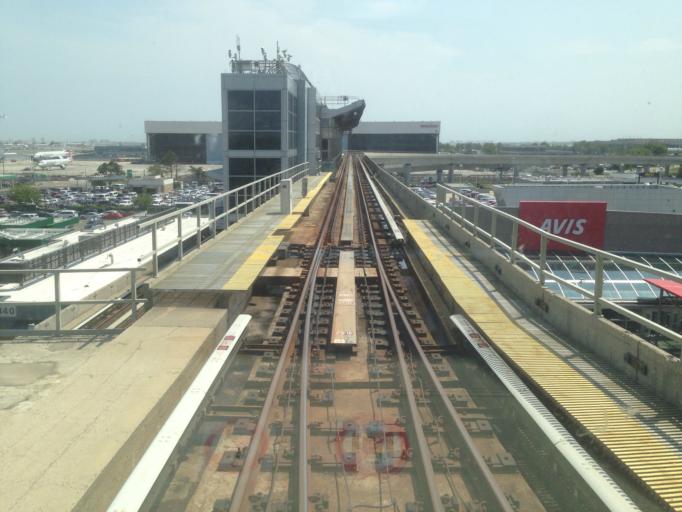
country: US
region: New York
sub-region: Queens County
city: Jamaica
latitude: 40.6607
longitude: -73.8036
